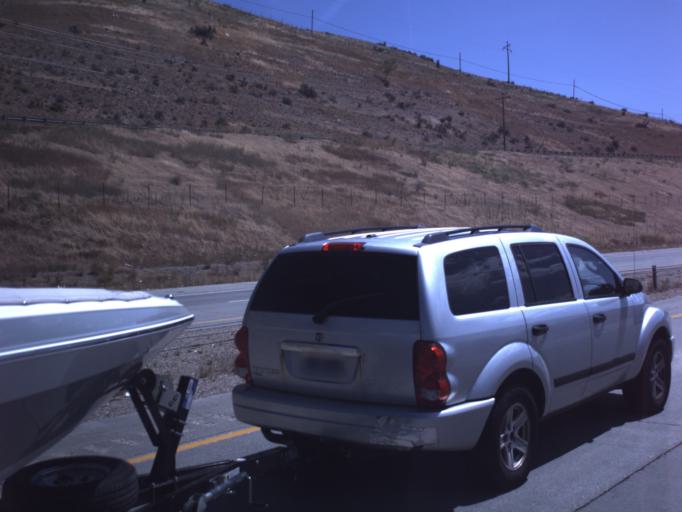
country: US
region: Utah
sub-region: Morgan County
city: Mountain Green
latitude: 41.1262
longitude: -111.7684
